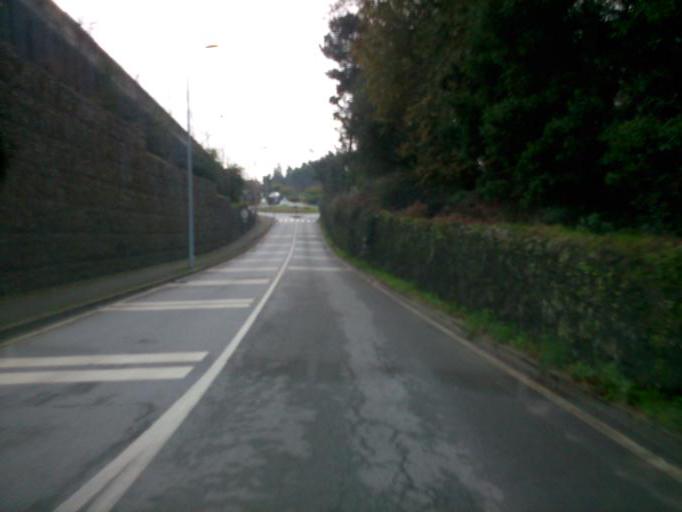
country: PT
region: Braga
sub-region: Barcelos
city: Barcelos
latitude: 41.5222
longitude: -8.6105
